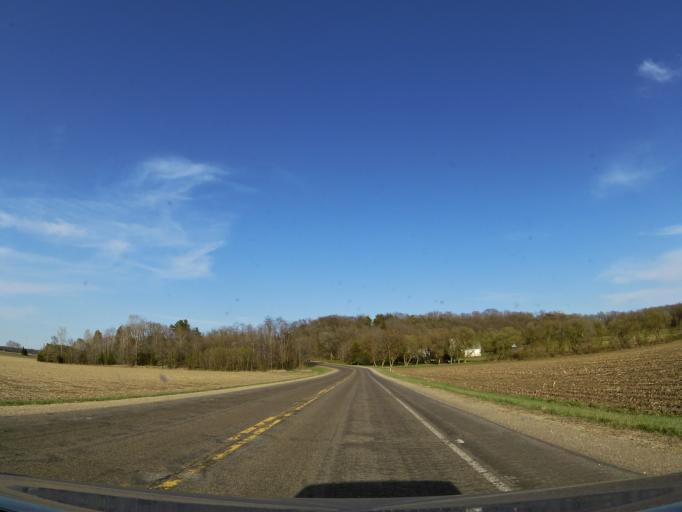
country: US
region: Wisconsin
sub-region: Pierce County
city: River Falls
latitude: 44.8626
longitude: -92.6779
